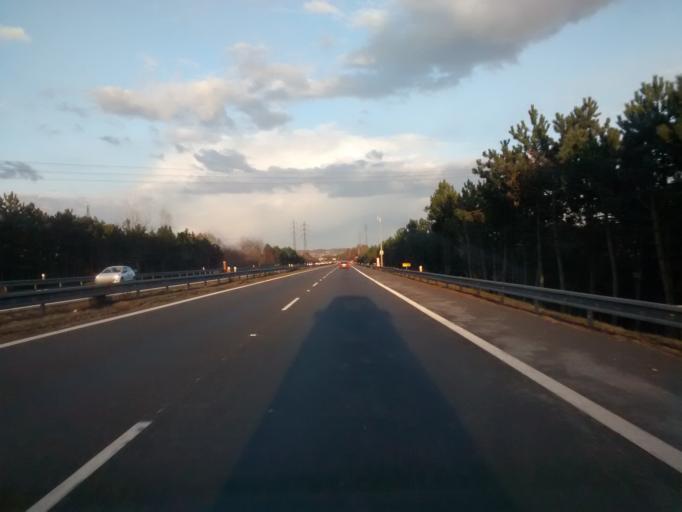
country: CZ
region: Central Bohemia
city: Celakovice
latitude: 50.1333
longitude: 14.7856
